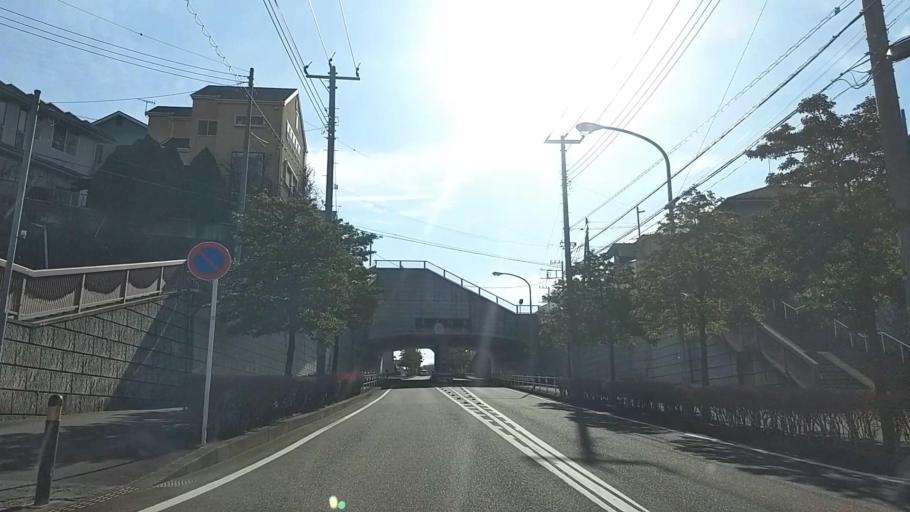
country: JP
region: Kanagawa
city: Hadano
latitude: 35.3658
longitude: 139.2263
